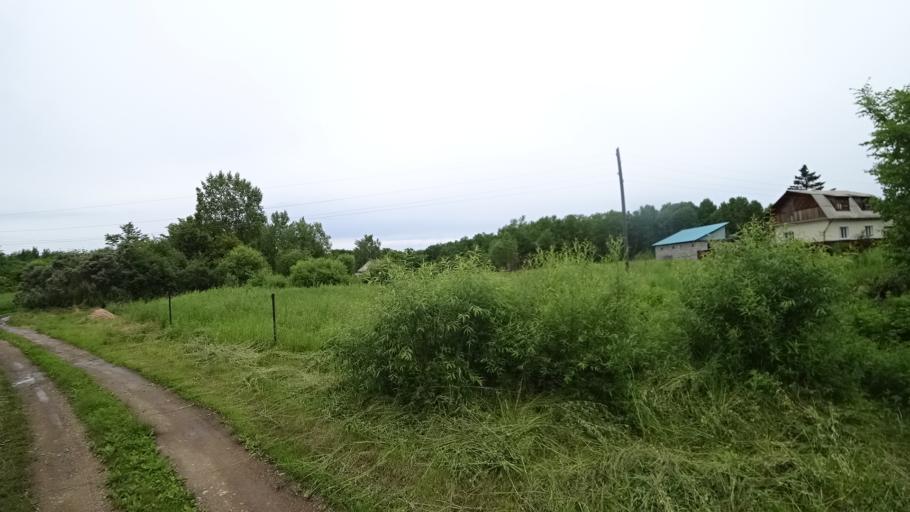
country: RU
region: Primorskiy
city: Novosysoyevka
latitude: 44.2039
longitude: 133.3283
